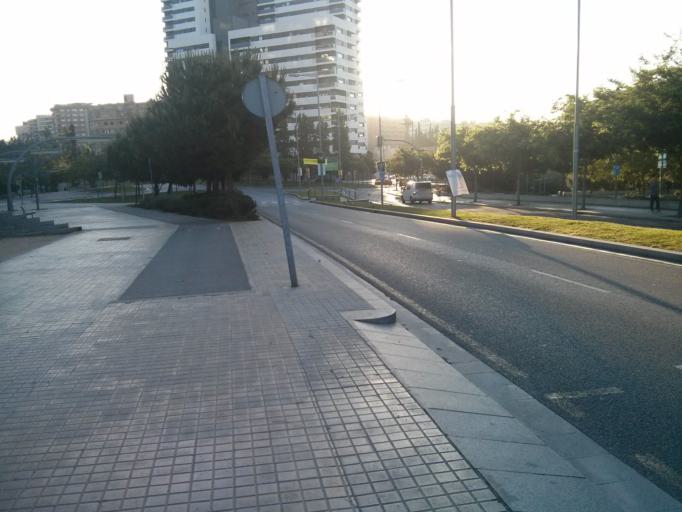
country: ES
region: Catalonia
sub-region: Provincia de Barcelona
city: L'Hospitalet de Llobregat
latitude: 41.3744
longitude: 2.1082
